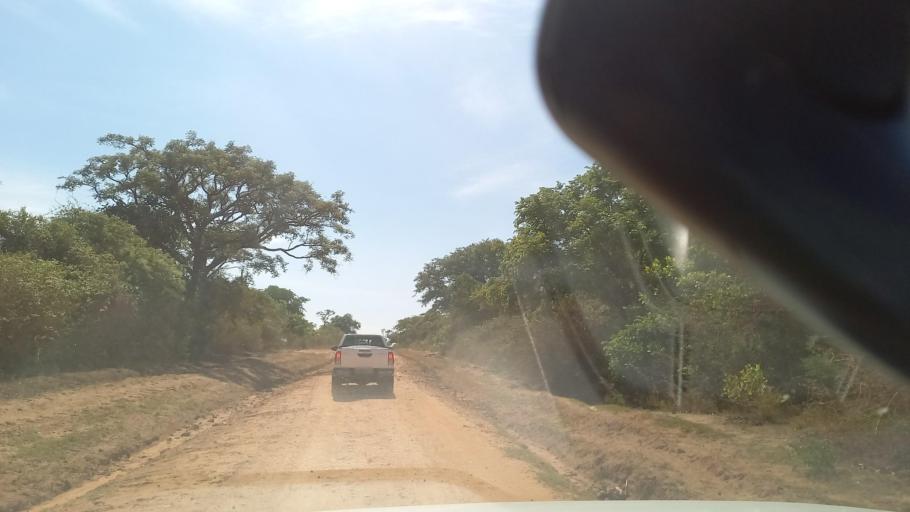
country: ZM
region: Southern
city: Mazabuka
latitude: -16.0407
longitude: 27.6208
